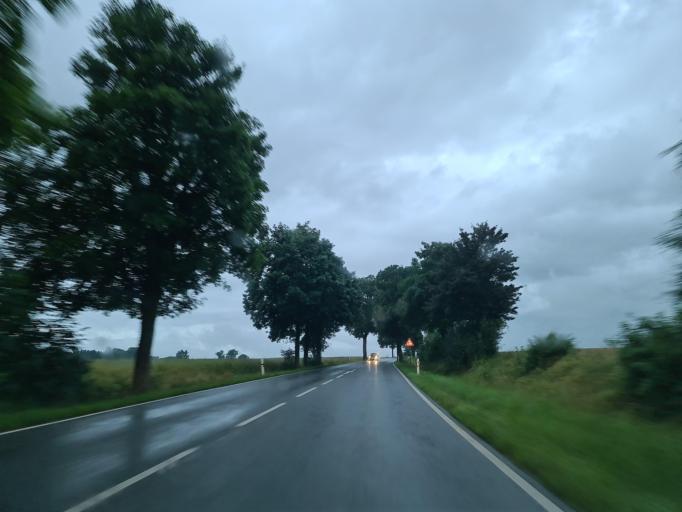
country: DE
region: Saxony
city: Neuensalz
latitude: 50.5152
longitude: 12.2405
